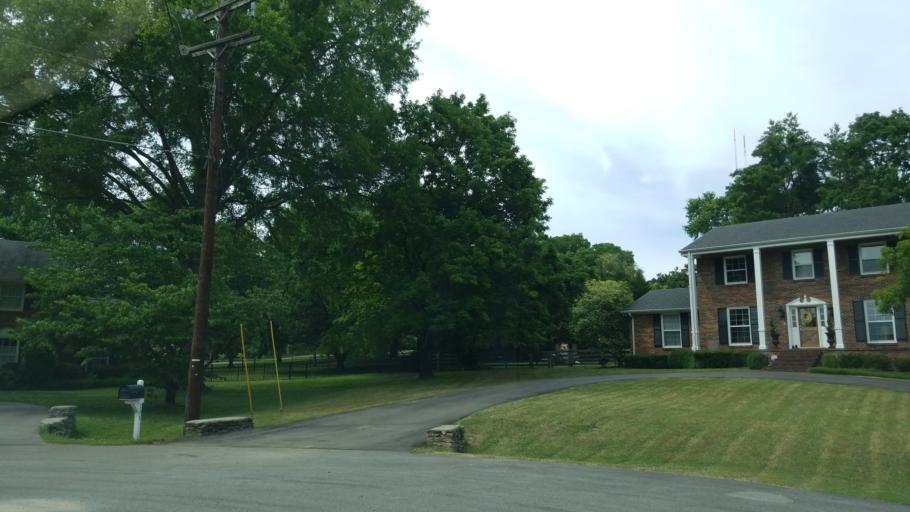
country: US
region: Tennessee
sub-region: Davidson County
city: Forest Hills
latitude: 36.0364
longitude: -86.8338
